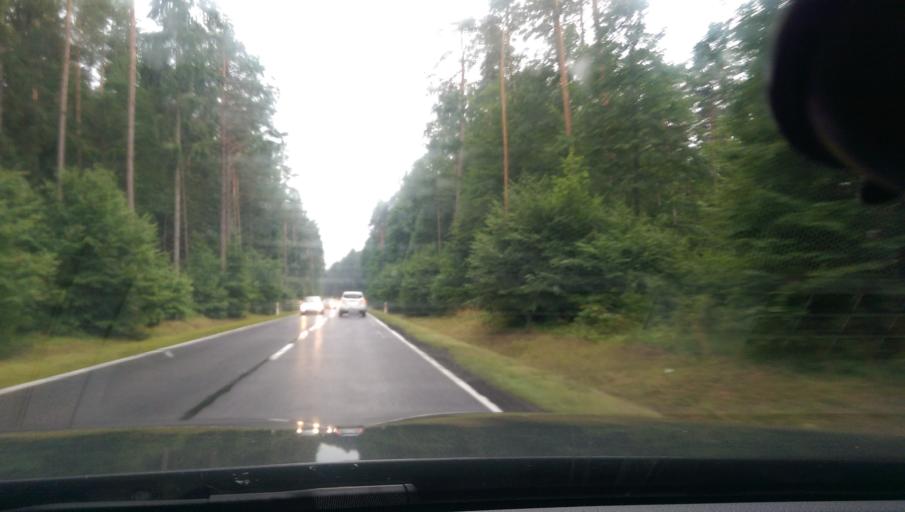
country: PL
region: Warmian-Masurian Voivodeship
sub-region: Powiat szczycienski
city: Szczytno
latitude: 53.5211
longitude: 20.9759
